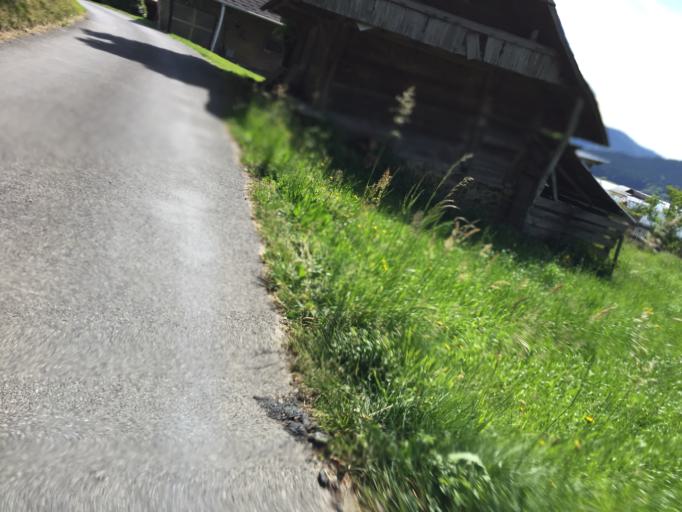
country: CH
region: Bern
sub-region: Bern-Mittelland District
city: Taegertschi
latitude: 46.8808
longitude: 7.5893
